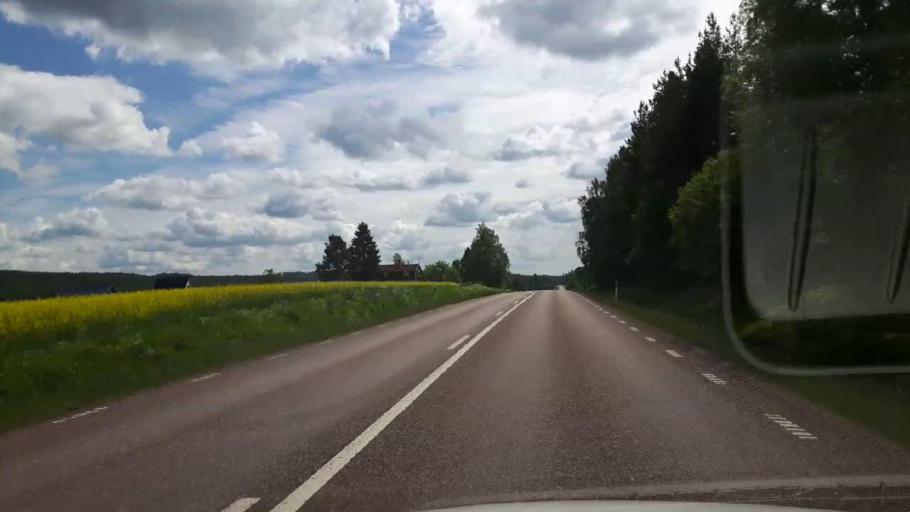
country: SE
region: Dalarna
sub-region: Hedemora Kommun
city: Hedemora
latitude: 60.3786
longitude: 15.9121
